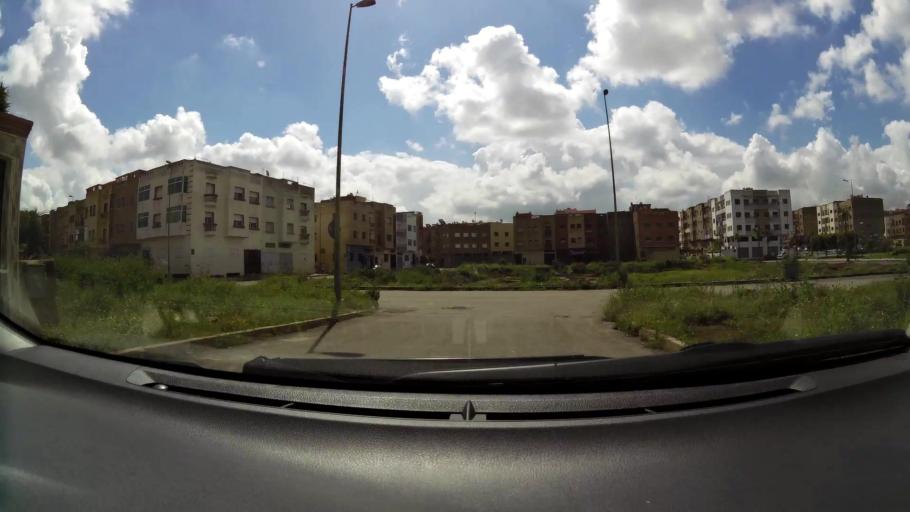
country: MA
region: Grand Casablanca
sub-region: Mediouna
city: Tit Mellil
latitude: 33.5545
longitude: -7.4844
